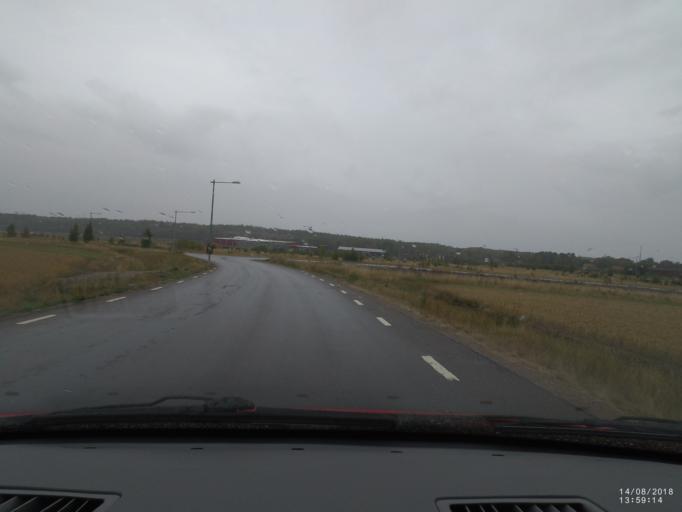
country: SE
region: Soedermanland
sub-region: Nykopings Kommun
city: Nykoping
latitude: 58.7525
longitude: 16.9716
